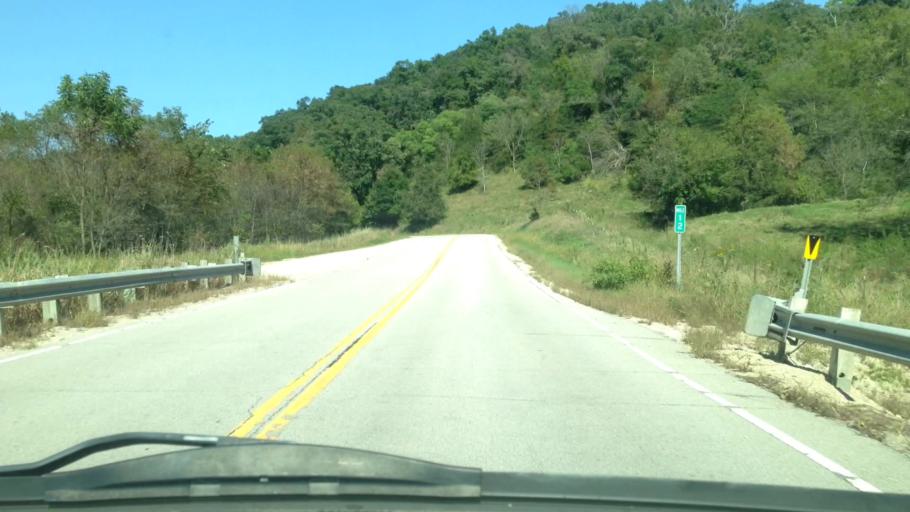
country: US
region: Minnesota
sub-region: Fillmore County
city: Rushford
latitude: 43.6767
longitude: -91.7897
